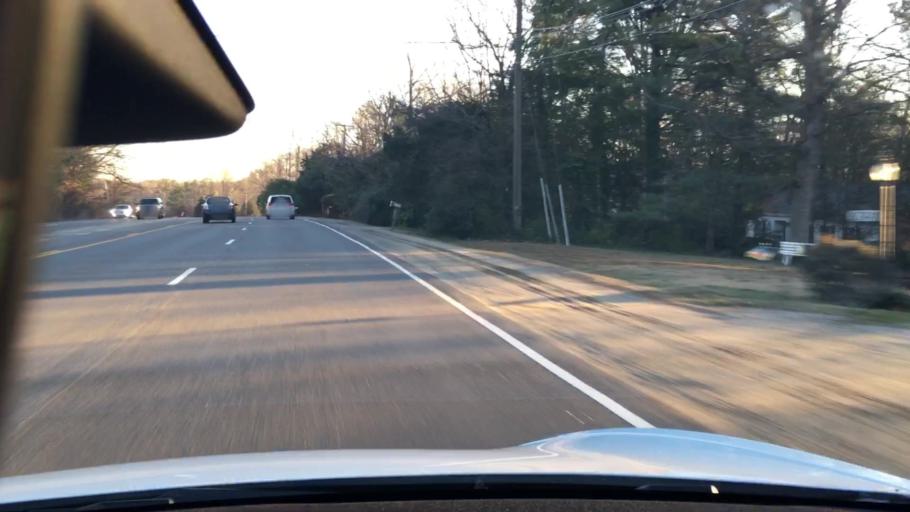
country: US
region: Virginia
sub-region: Chesterfield County
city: Bon Air
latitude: 37.5397
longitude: -77.5582
